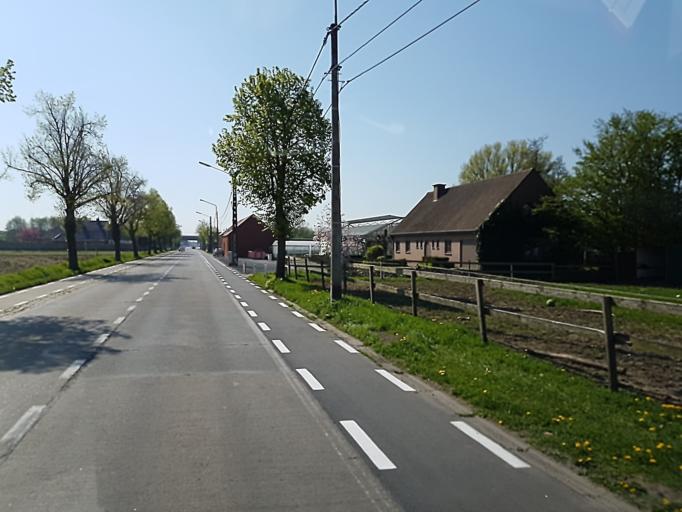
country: BE
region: Flanders
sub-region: Provincie West-Vlaanderen
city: Menen
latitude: 50.8195
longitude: 3.1190
